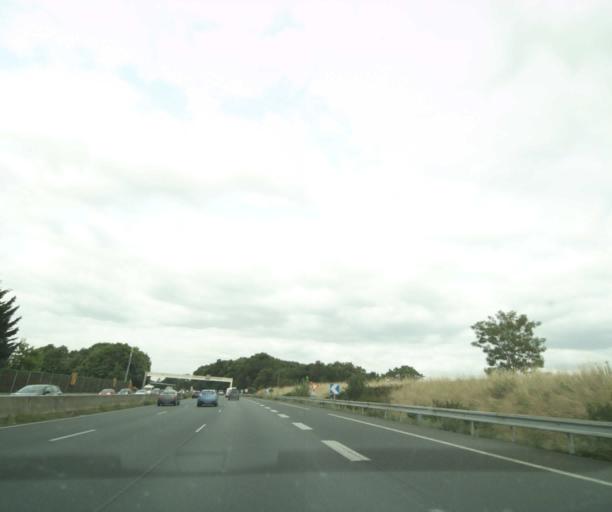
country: FR
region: Centre
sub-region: Departement d'Indre-et-Loire
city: Rochecorbon
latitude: 47.4102
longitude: 0.7263
